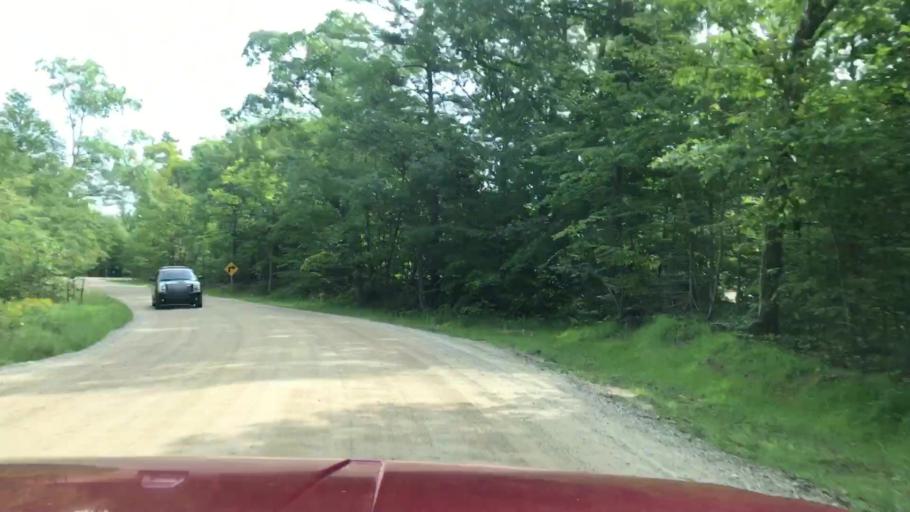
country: US
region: Michigan
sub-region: Charlevoix County
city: Charlevoix
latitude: 45.7476
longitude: -85.5403
